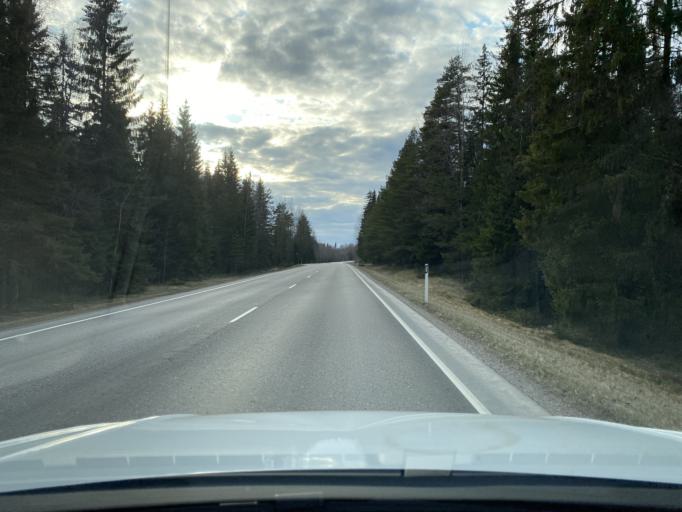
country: FI
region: Haeme
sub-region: Haemeenlinna
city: Renko
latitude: 60.7860
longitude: 24.1416
